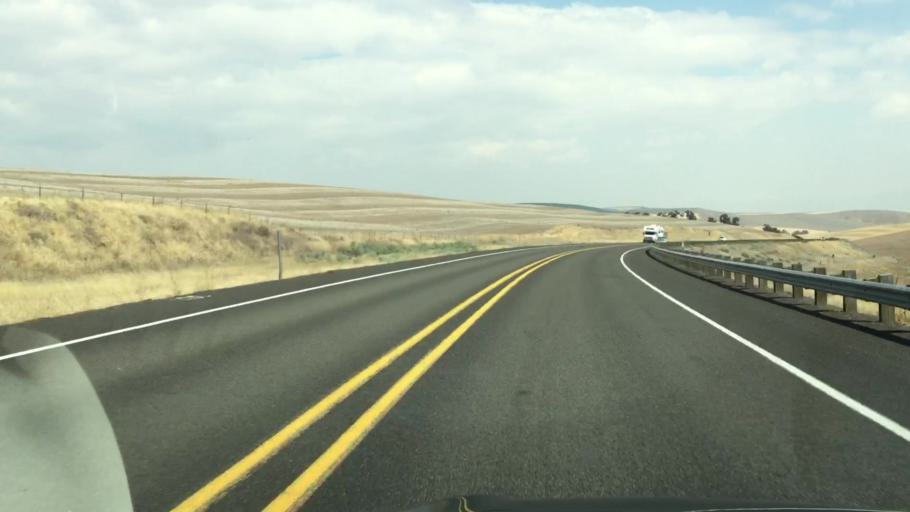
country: US
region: Oregon
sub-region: Wasco County
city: The Dalles
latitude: 45.4690
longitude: -121.1217
